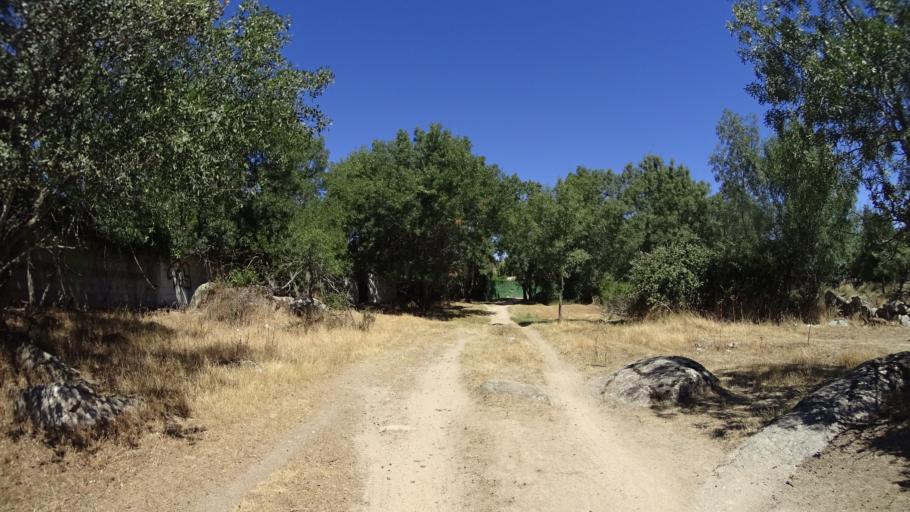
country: ES
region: Madrid
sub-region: Provincia de Madrid
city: Alpedrete
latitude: 40.6609
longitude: -4.0482
